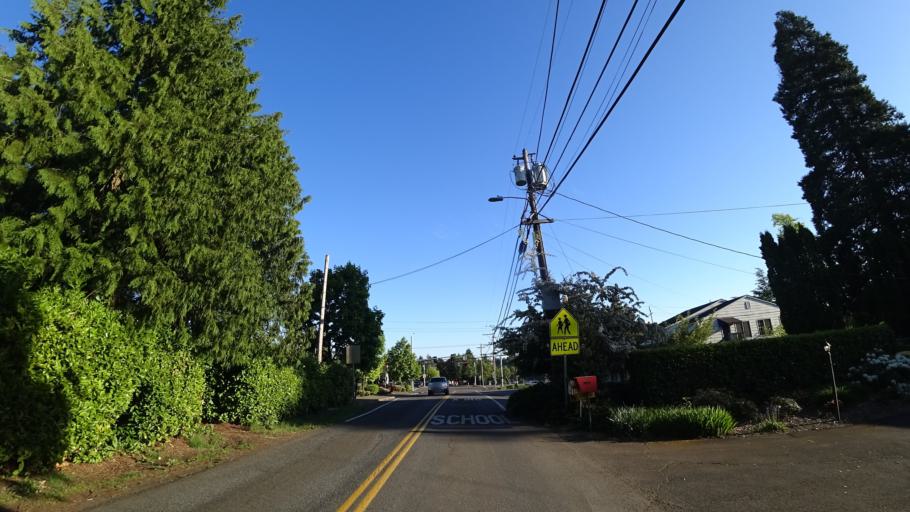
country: US
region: Oregon
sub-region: Washington County
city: Raleigh Hills
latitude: 45.4872
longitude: -122.7682
